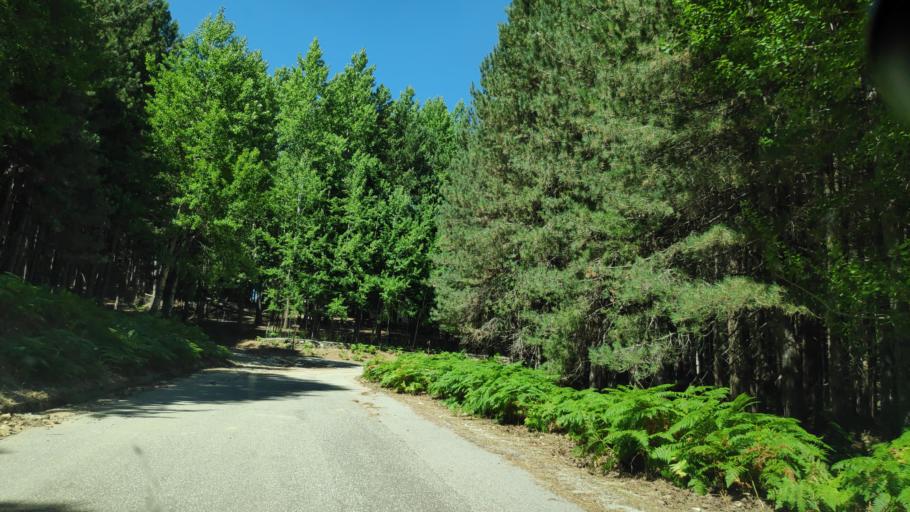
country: IT
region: Calabria
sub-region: Provincia di Reggio Calabria
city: Africo Vecchio
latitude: 38.0363
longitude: 15.9503
